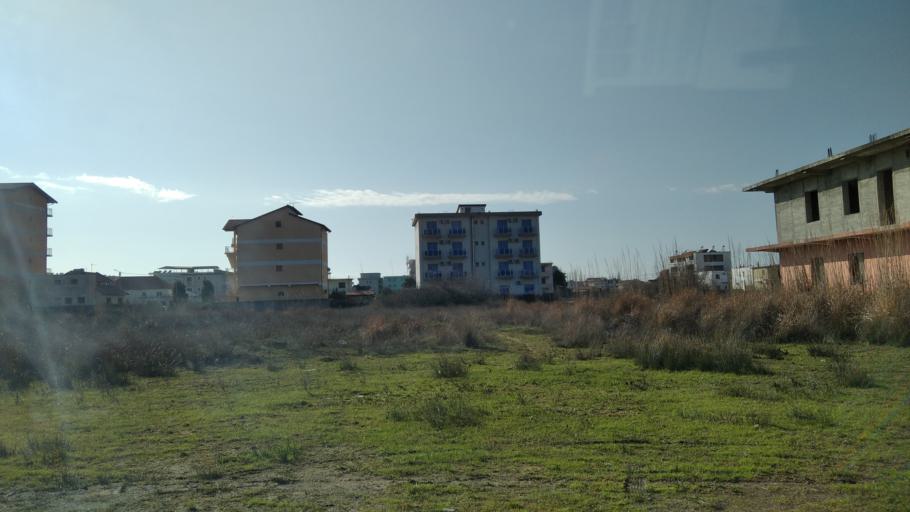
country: AL
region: Shkoder
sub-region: Rrethi i Shkodres
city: Velipoje
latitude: 41.8643
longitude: 19.4353
